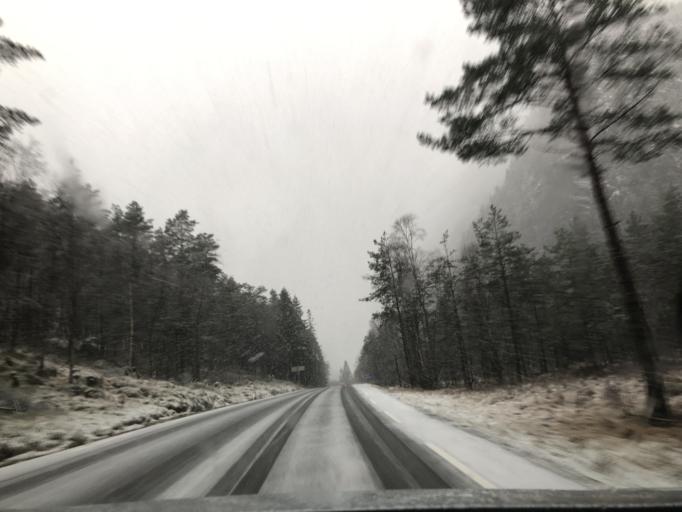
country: NO
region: Rogaland
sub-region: Hjelmeland
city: Hjelmelandsvagen
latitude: 59.3109
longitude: 6.3232
